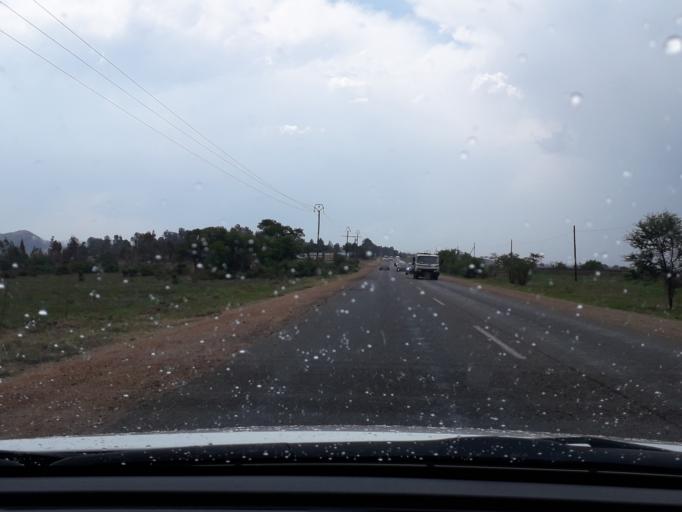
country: ZA
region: Gauteng
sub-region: West Rand District Municipality
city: Muldersdriseloop
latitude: -26.0062
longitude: 27.8583
